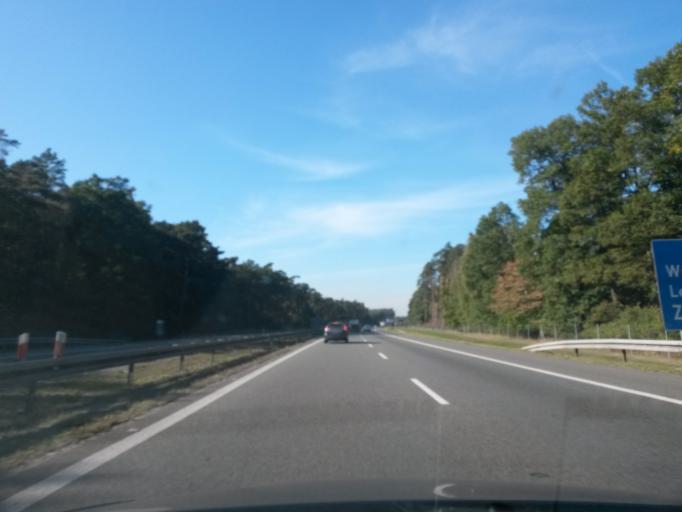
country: PL
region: Opole Voivodeship
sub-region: Powiat opolski
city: Proszkow
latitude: 50.5344
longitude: 17.9070
